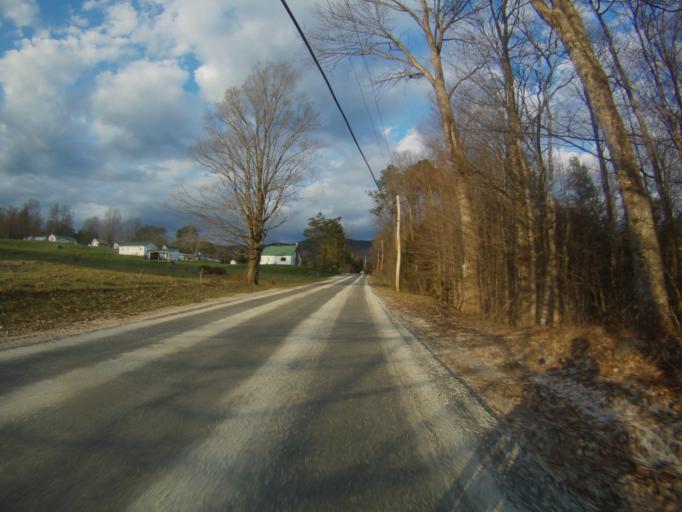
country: US
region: Vermont
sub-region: Rutland County
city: Brandon
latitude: 43.8542
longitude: -73.0132
